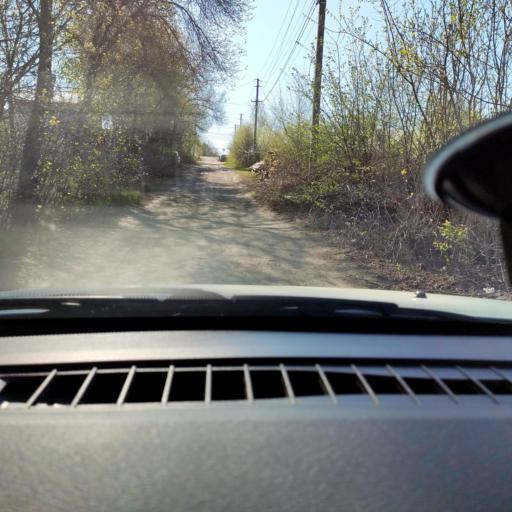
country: RU
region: Samara
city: Dubovyy Umet
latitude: 53.0828
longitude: 50.3887
